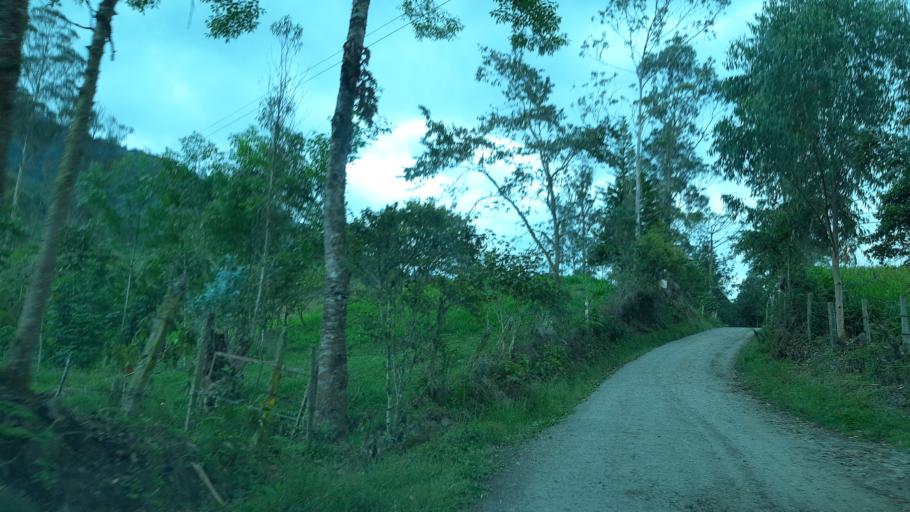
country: CO
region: Boyaca
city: Garagoa
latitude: 5.1211
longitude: -73.3445
